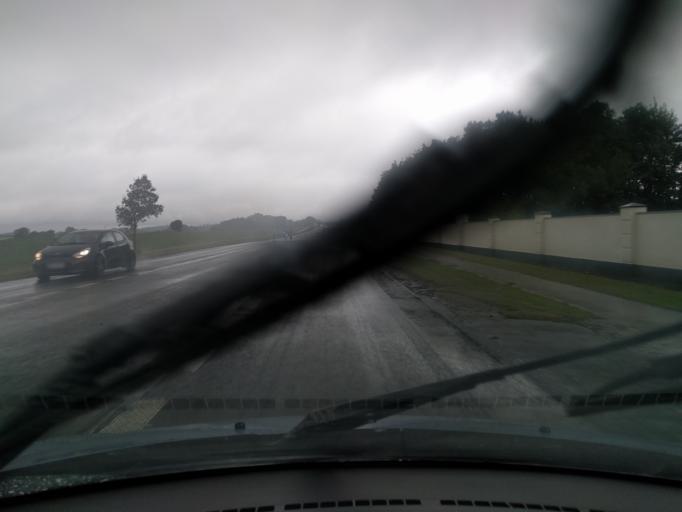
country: DK
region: Zealand
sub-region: Naestved Kommune
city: Naestved
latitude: 55.1592
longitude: 11.8189
